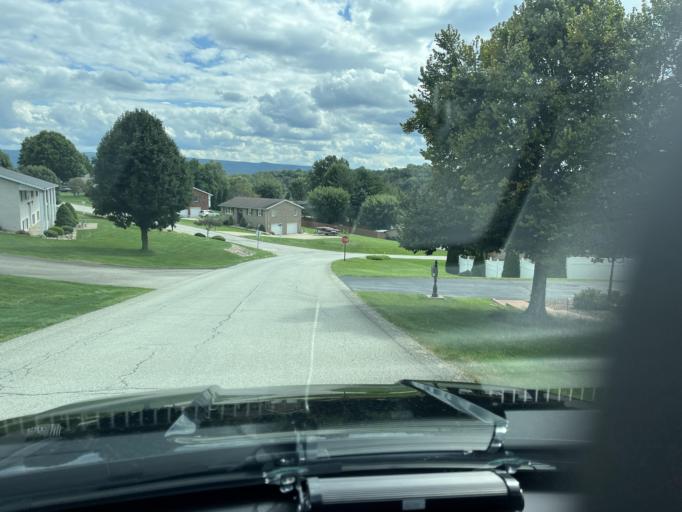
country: US
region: Pennsylvania
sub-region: Fayette County
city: South Uniontown
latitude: 39.8977
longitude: -79.7609
